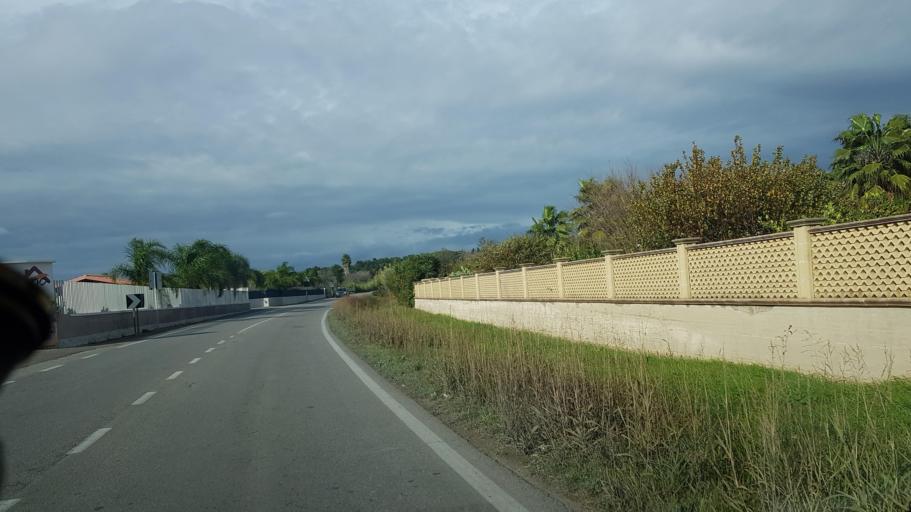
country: IT
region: Apulia
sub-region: Provincia di Brindisi
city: Oria
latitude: 40.4913
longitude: 17.6369
